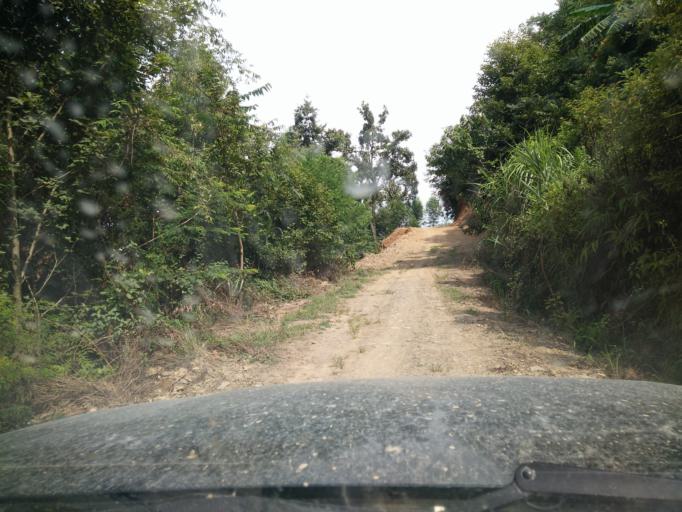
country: CN
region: Guangxi Zhuangzu Zizhiqu
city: Leli
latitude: 24.7645
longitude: 105.9035
